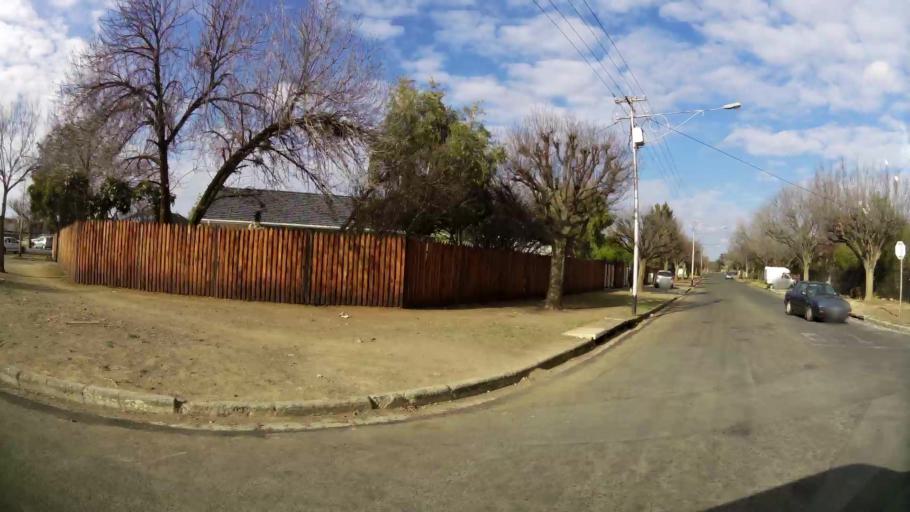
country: ZA
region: Orange Free State
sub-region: Mangaung Metropolitan Municipality
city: Bloemfontein
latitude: -29.0833
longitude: 26.2135
